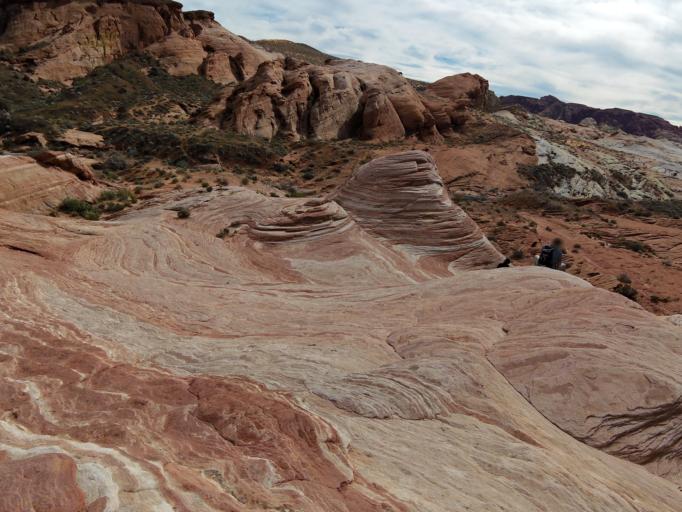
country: US
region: Nevada
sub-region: Clark County
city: Moapa Valley
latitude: 36.4830
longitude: -114.5224
